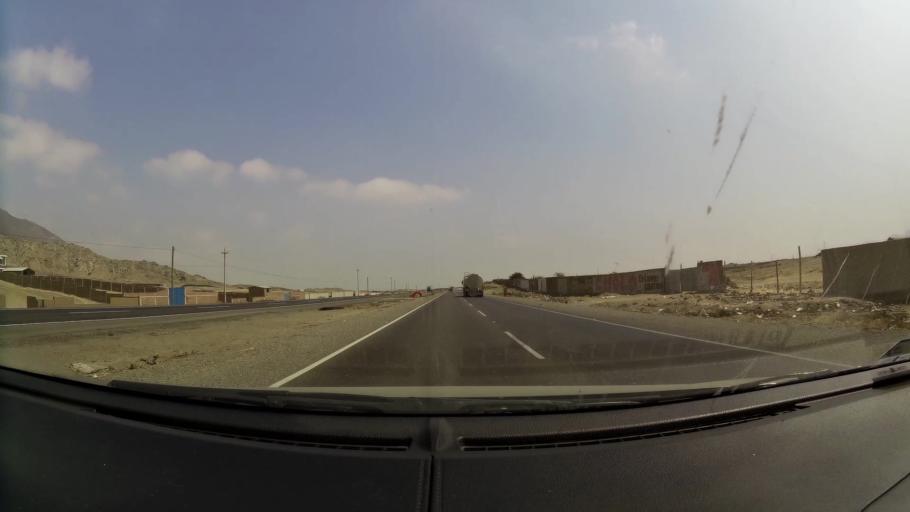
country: PE
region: La Libertad
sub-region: Ascope
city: Chicama
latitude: -7.9302
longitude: -79.1042
